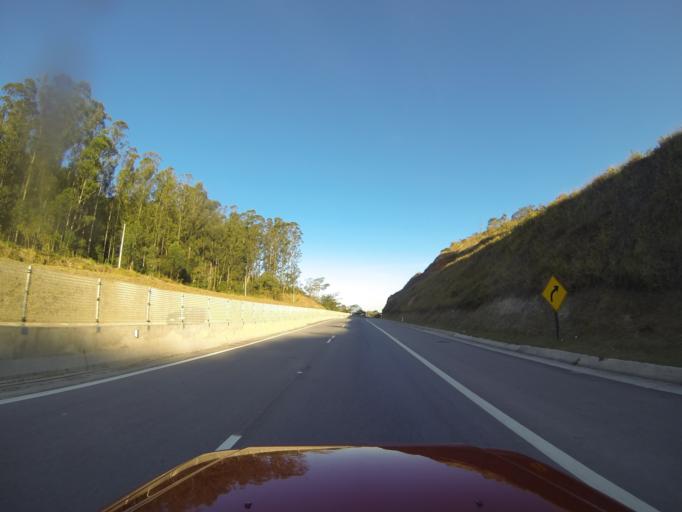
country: BR
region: Sao Paulo
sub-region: Santa Branca
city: Santa Branca
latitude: -23.2954
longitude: -45.7799
